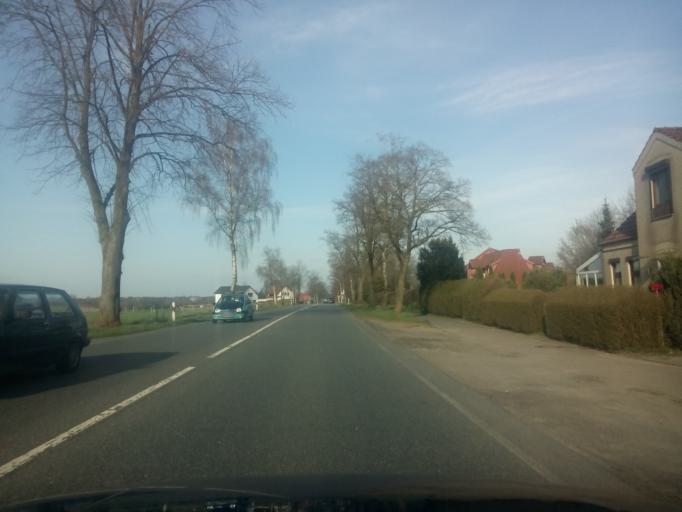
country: DE
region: Lower Saxony
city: Ritterhude
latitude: 53.2068
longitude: 8.7582
